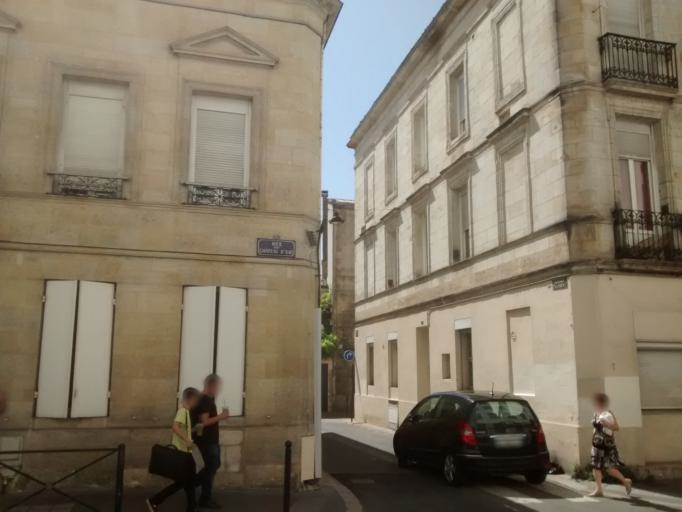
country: FR
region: Aquitaine
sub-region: Departement de la Gironde
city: Bordeaux
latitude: 44.8411
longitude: -0.5834
